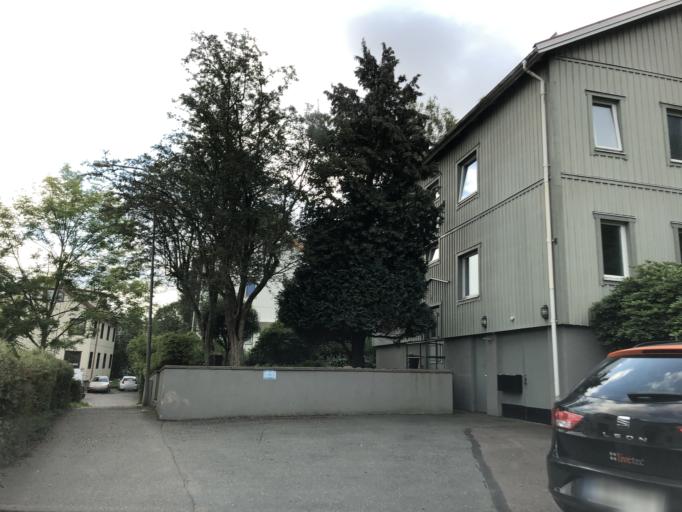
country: SE
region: Vaestra Goetaland
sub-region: Goteborg
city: Goeteborg
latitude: 57.7230
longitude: 12.0164
